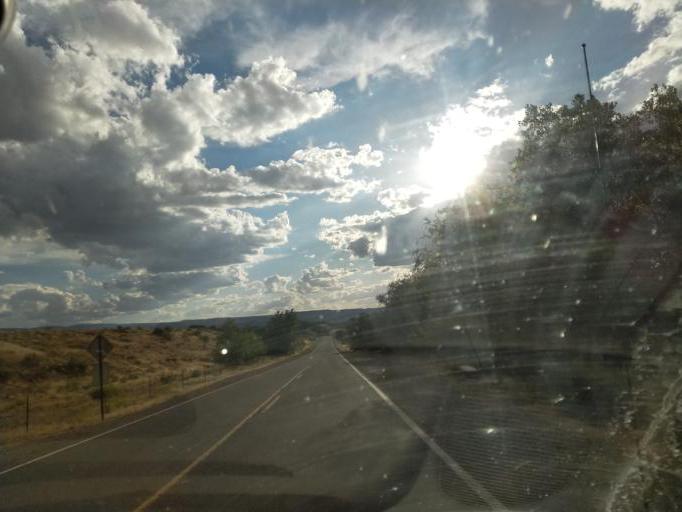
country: US
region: Colorado
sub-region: Mesa County
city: Clifton
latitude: 39.0555
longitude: -108.4524
